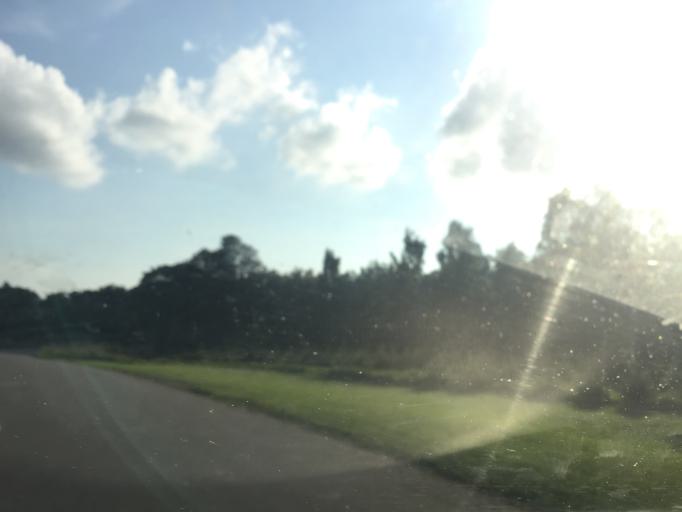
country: DK
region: Zealand
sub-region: Kalundborg Kommune
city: Svebolle
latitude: 55.6443
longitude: 11.2295
